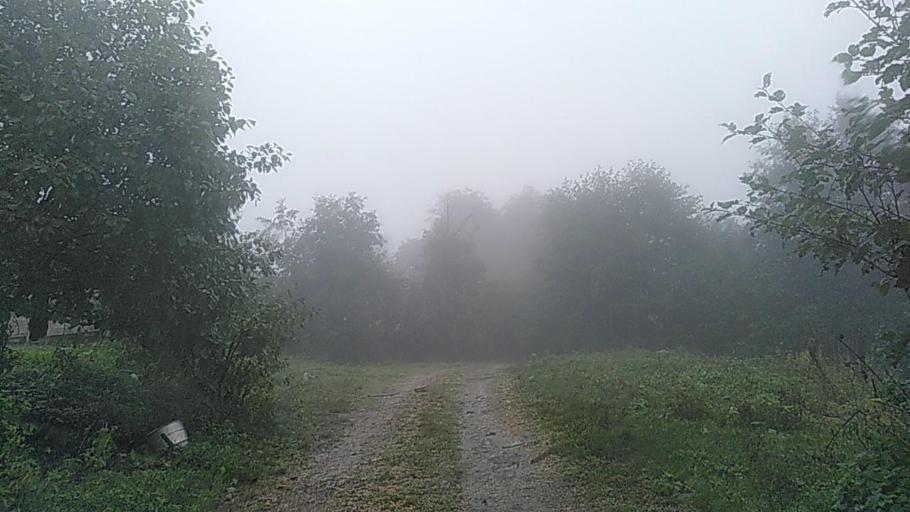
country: RU
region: Kabardino-Balkariya
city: Belaya Rechka
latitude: 43.3569
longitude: 43.4021
